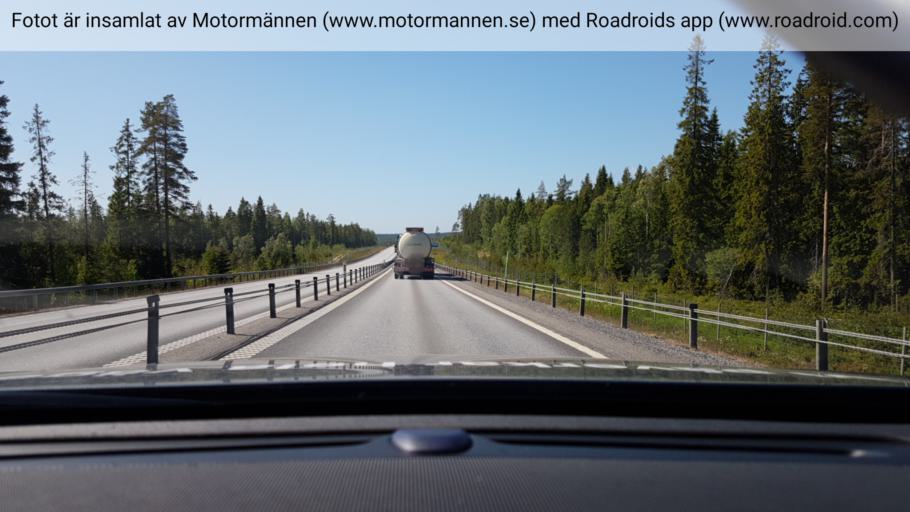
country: SE
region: Vaesterbotten
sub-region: Umea Kommun
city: Roback
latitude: 63.7091
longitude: 20.0529
